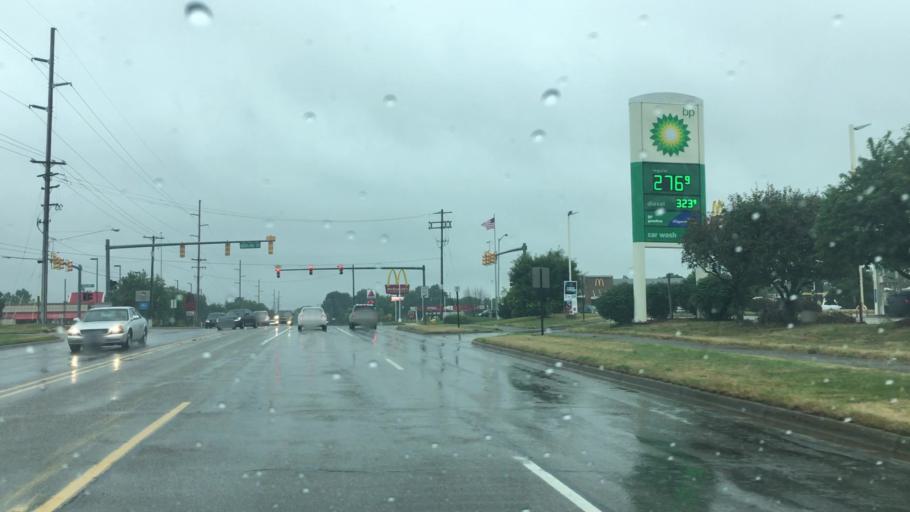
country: US
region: Michigan
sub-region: Ottawa County
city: Hudsonville
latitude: 42.8518
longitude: -85.8612
